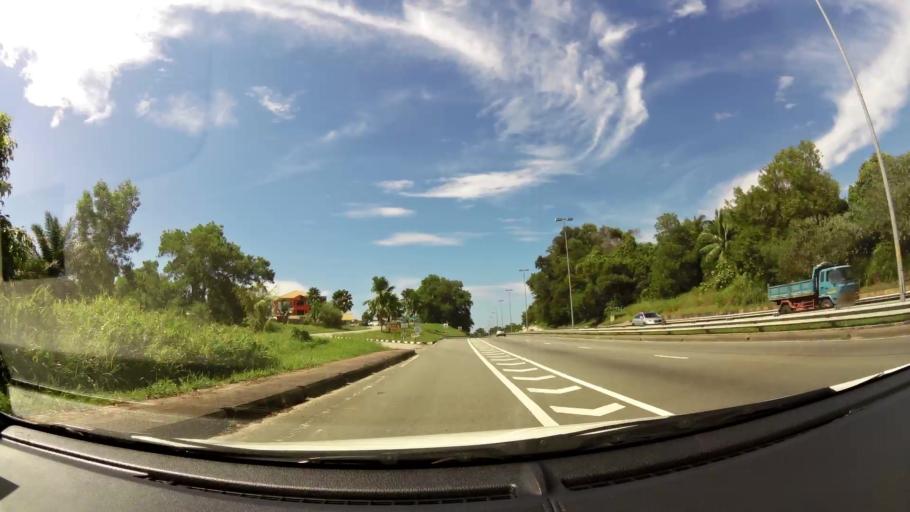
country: BN
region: Brunei and Muara
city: Bandar Seri Begawan
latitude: 4.9697
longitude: 114.9529
